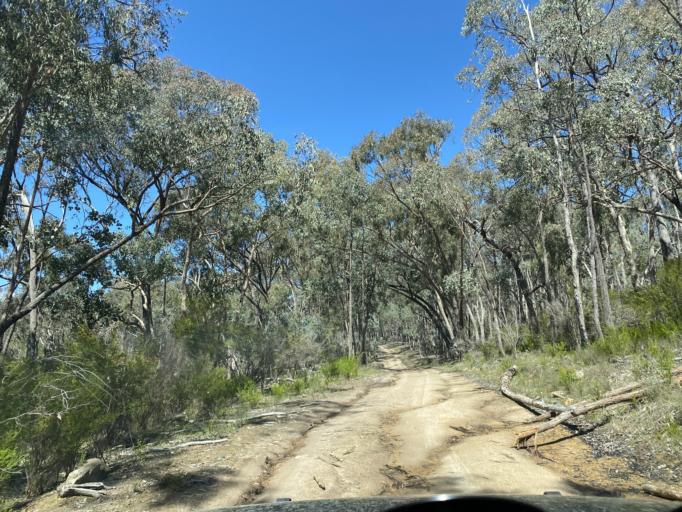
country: AU
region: Victoria
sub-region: Benalla
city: Benalla
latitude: -36.6995
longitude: 146.1521
